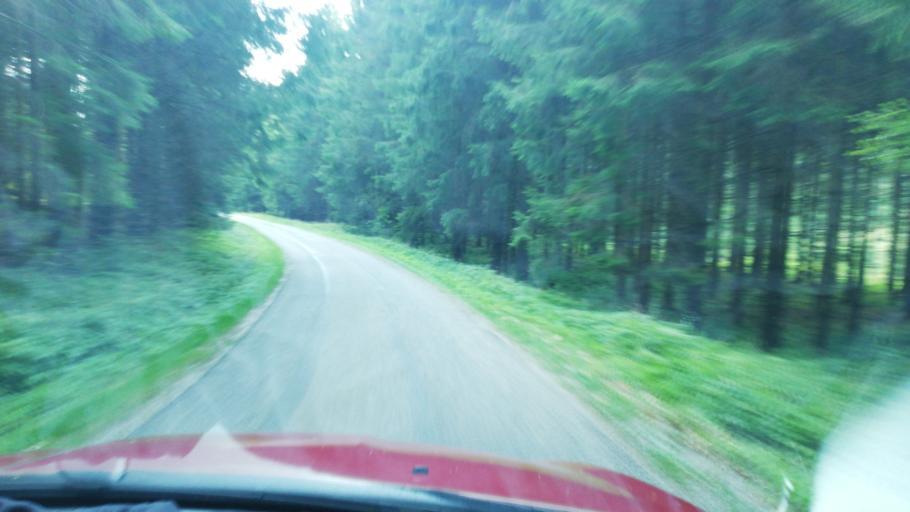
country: AT
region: Lower Austria
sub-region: Politischer Bezirk Zwettl
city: Langschlag
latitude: 48.4830
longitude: 14.8408
